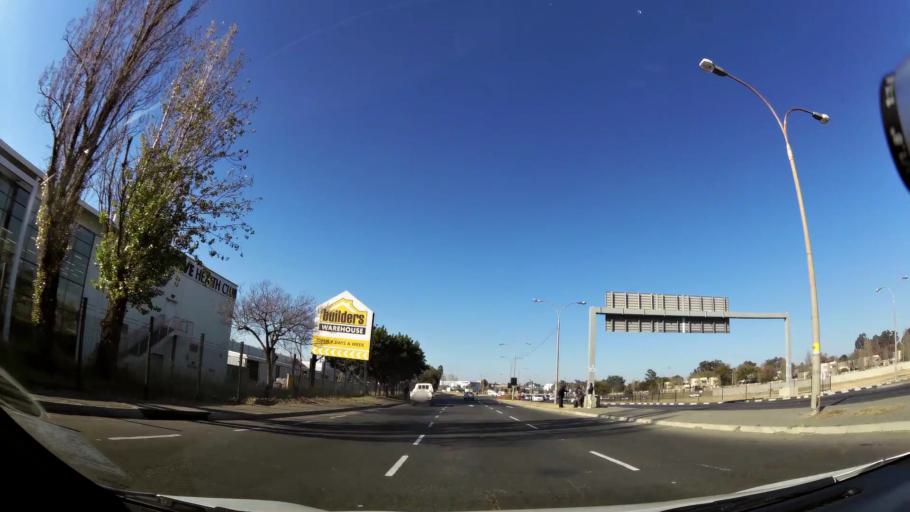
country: ZA
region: Gauteng
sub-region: Ekurhuleni Metropolitan Municipality
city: Germiston
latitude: -26.2761
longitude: 28.1235
